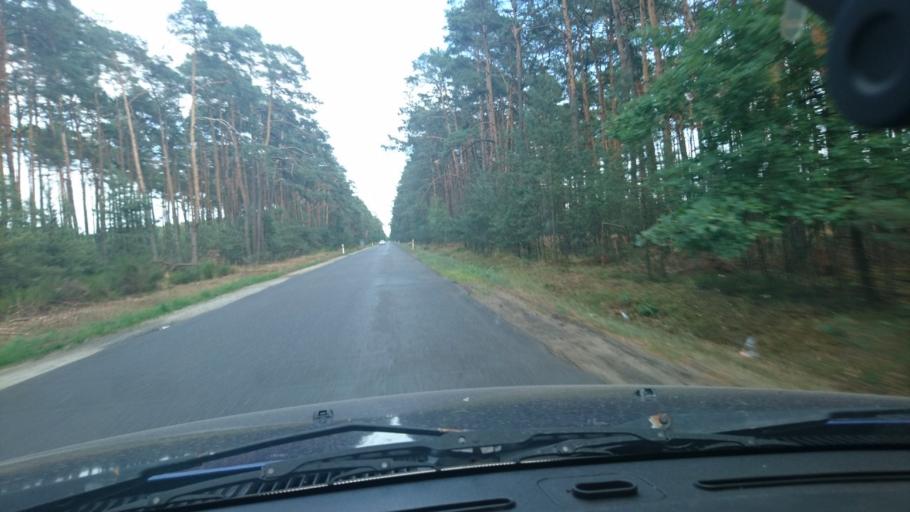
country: PL
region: Greater Poland Voivodeship
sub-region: Powiat ostrzeszowski
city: Kobyla Gora
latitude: 51.4389
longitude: 17.8404
